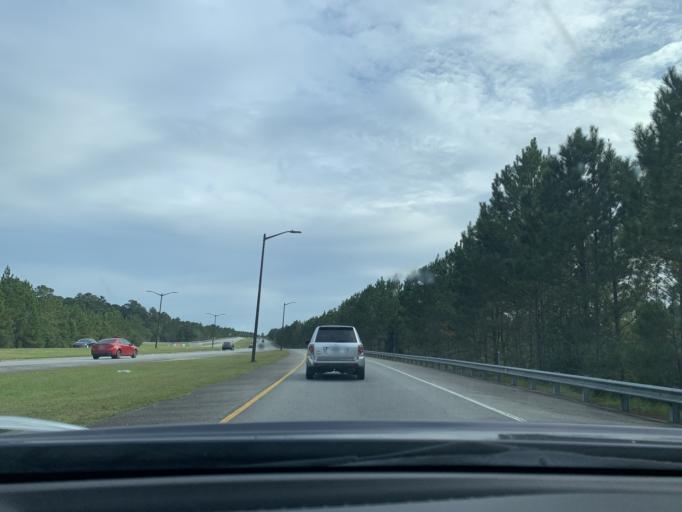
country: US
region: Georgia
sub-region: Chatham County
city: Pooler
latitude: 32.1174
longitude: -81.2695
